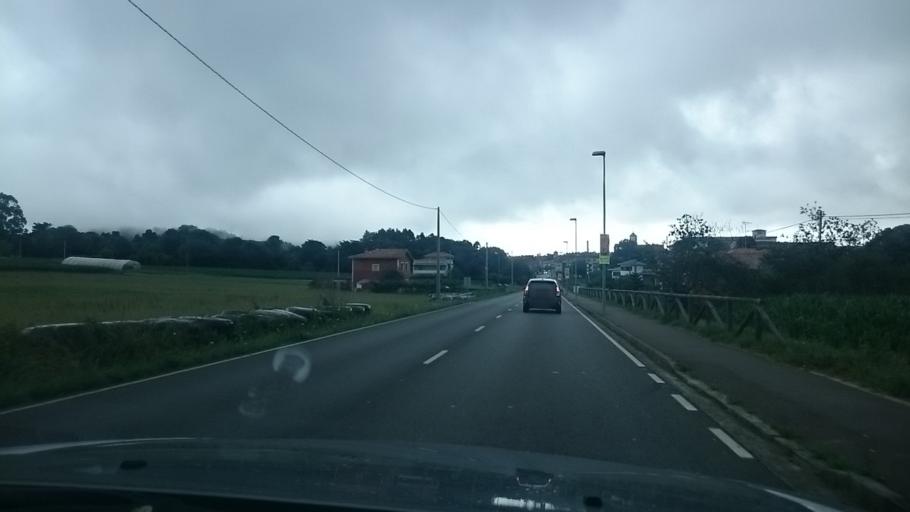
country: ES
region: Asturias
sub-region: Province of Asturias
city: Carrena
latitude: 43.4197
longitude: -4.8700
